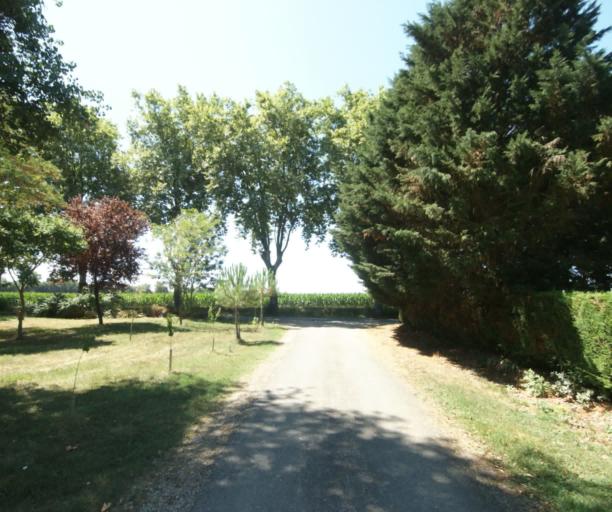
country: FR
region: Midi-Pyrenees
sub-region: Departement de la Haute-Garonne
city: Revel
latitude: 43.4987
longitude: 1.9603
